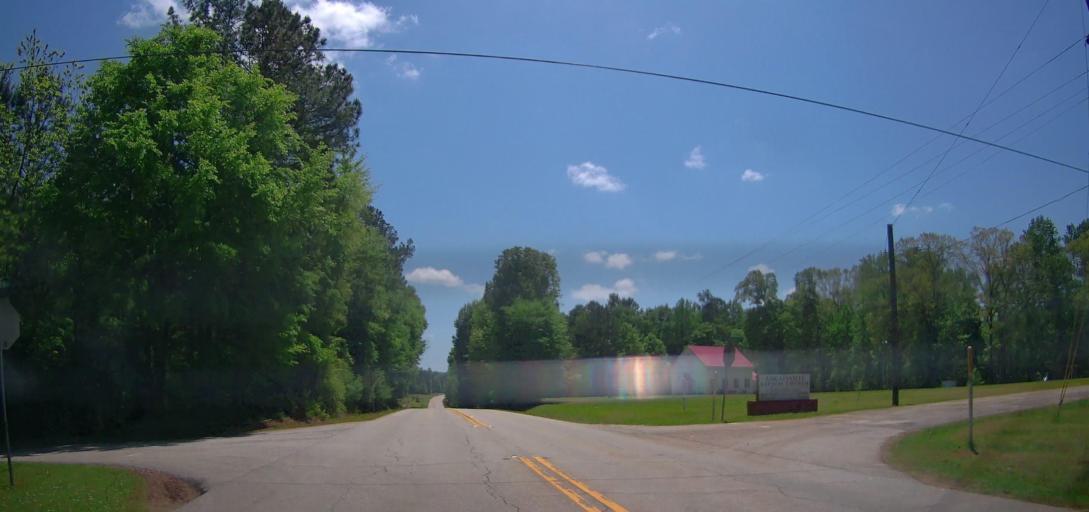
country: US
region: Georgia
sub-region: Jasper County
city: Monticello
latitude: 33.2237
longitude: -83.6725
